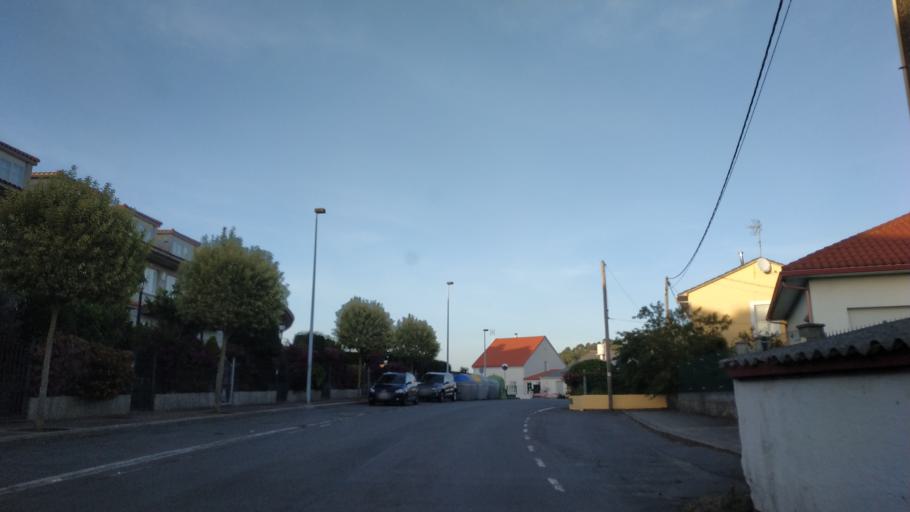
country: ES
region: Galicia
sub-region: Provincia da Coruna
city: Oleiros
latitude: 43.3633
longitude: -8.3388
